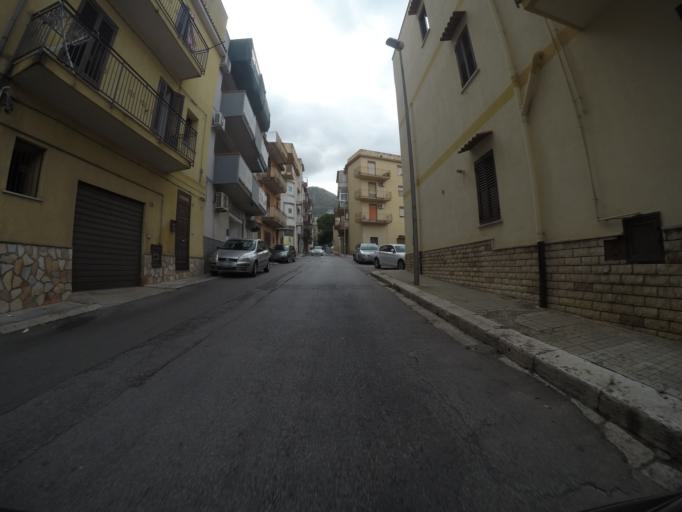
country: IT
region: Sicily
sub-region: Palermo
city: Carini
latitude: 38.1348
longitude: 13.1868
